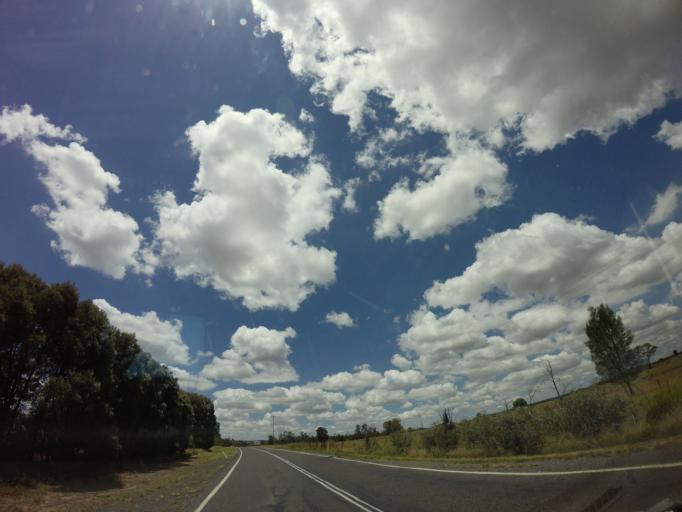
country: AU
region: Queensland
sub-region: Western Downs
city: Dalby
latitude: -27.9697
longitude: 151.1120
